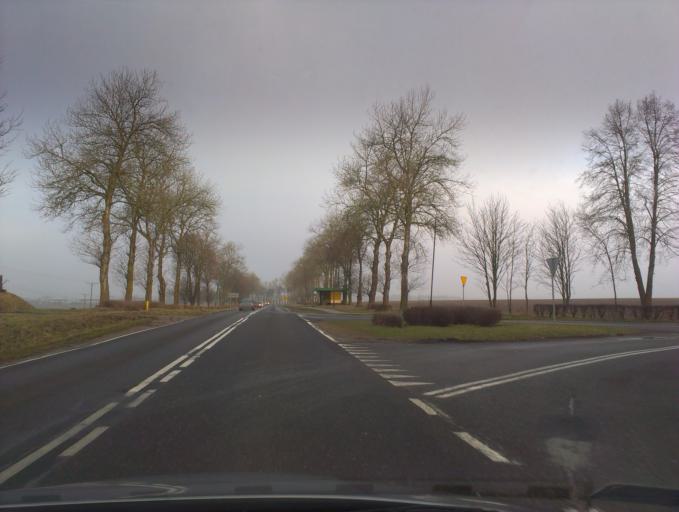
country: PL
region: West Pomeranian Voivodeship
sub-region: Koszalin
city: Koszalin
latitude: 54.1493
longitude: 16.2447
